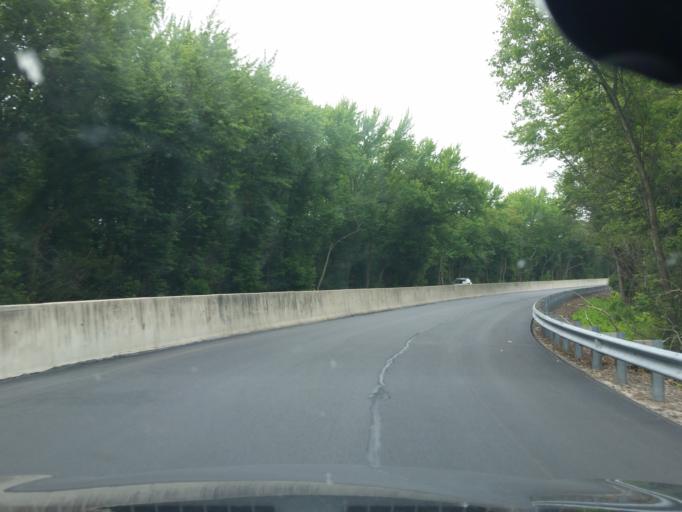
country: US
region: Pennsylvania
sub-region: Perry County
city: Duncannon
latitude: 40.4217
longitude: -77.0073
